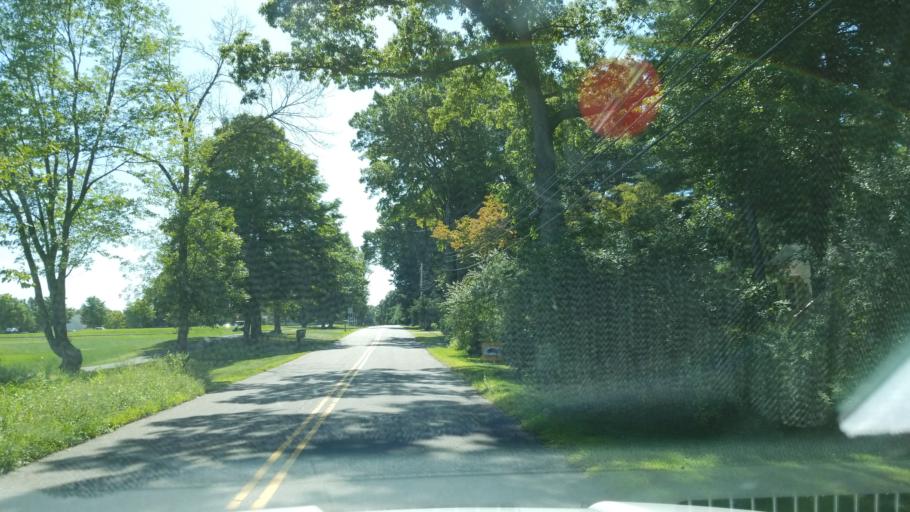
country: US
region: Connecticut
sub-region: Hartford County
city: Tariffville
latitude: 41.8586
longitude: -72.7606
